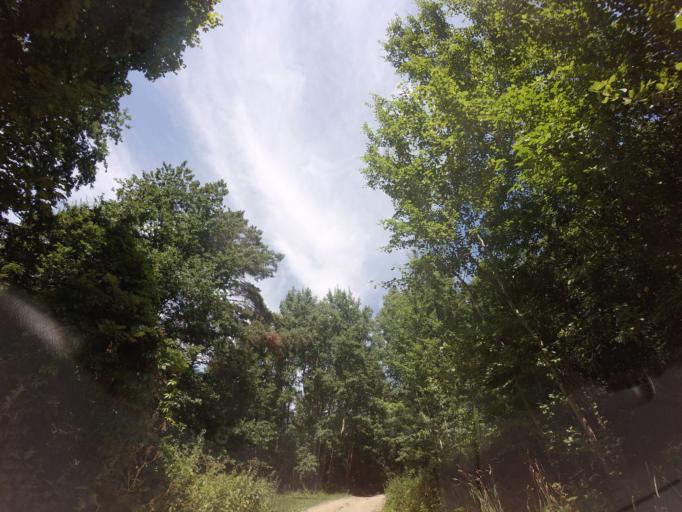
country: PL
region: West Pomeranian Voivodeship
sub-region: Powiat choszczenski
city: Recz
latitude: 53.2669
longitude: 15.5295
